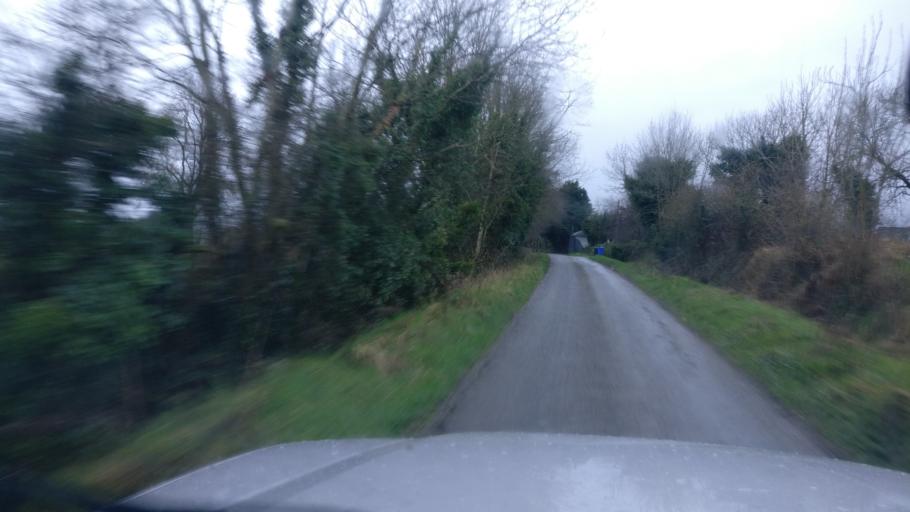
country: IE
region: Connaught
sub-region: County Galway
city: Ballinasloe
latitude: 53.2583
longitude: -8.3900
